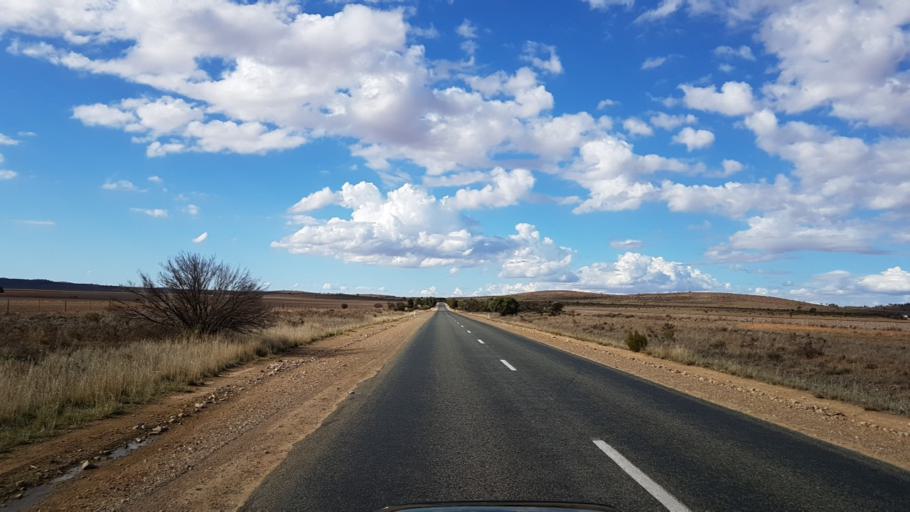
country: AU
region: South Australia
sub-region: Peterborough
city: Peterborough
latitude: -32.9647
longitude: 138.8798
